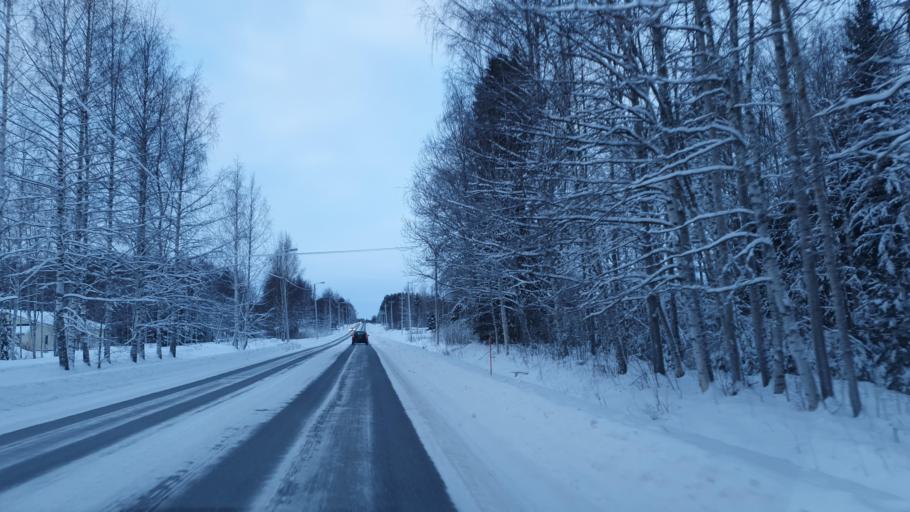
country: FI
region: Northern Ostrobothnia
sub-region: Oulu
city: Haukipudas
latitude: 65.1973
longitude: 25.3869
